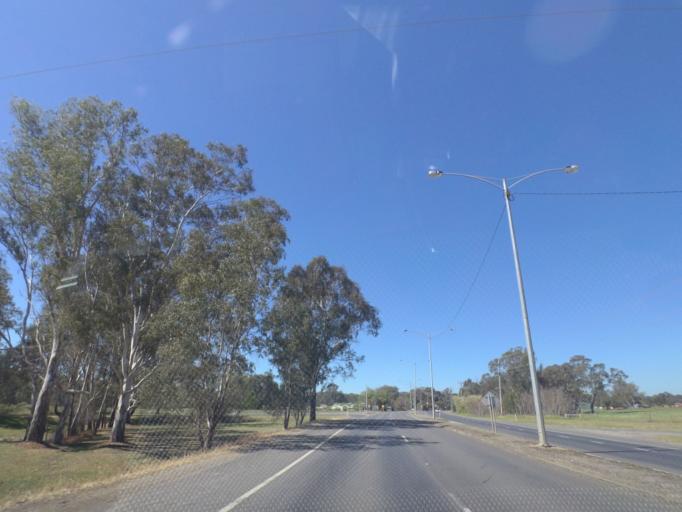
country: AU
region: Victoria
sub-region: Murrindindi
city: Kinglake West
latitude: -37.0228
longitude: 145.1152
